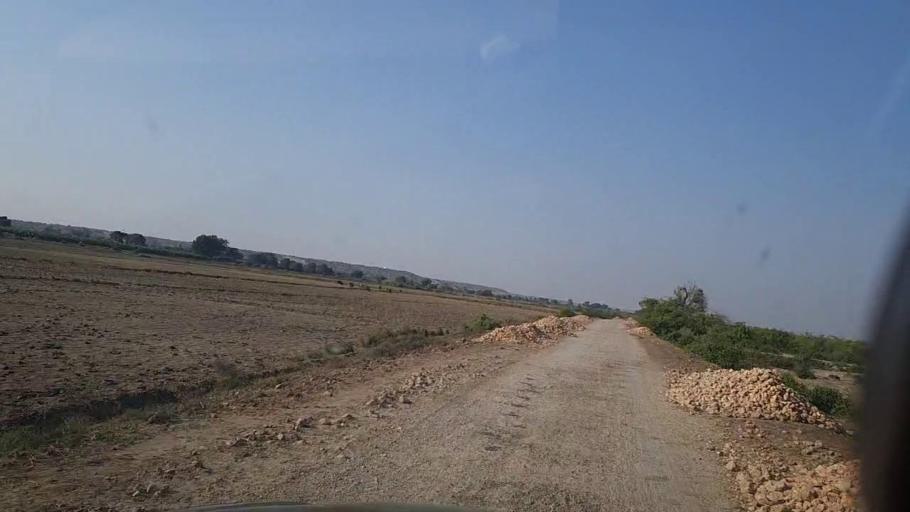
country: PK
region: Sindh
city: Thatta
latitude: 24.5870
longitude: 67.8769
